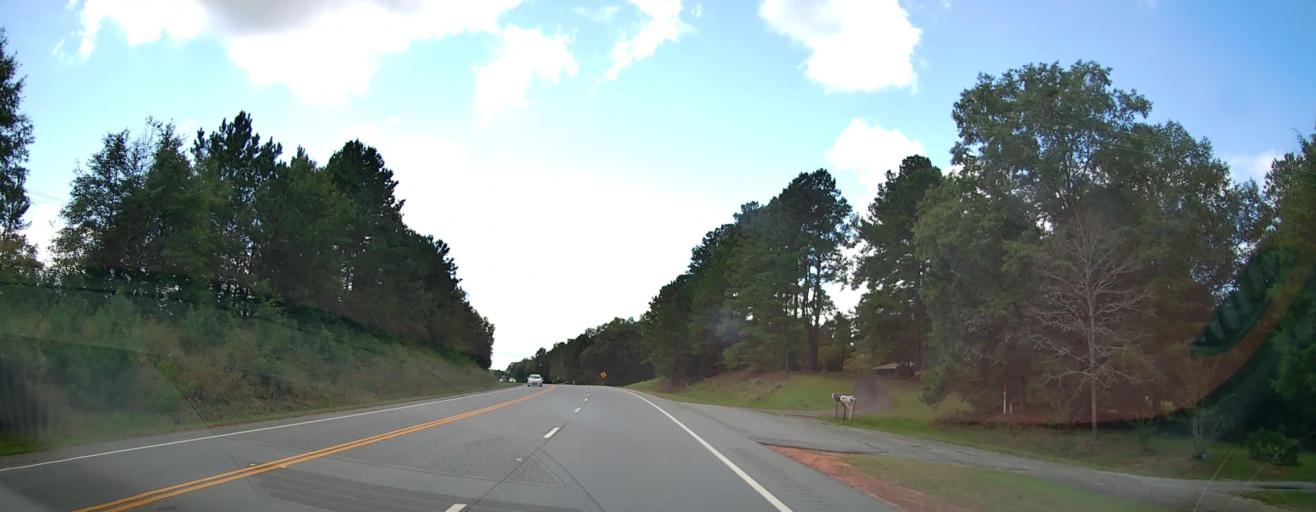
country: US
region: Georgia
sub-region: Baldwin County
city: Milledgeville
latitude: 33.0728
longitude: -83.3474
